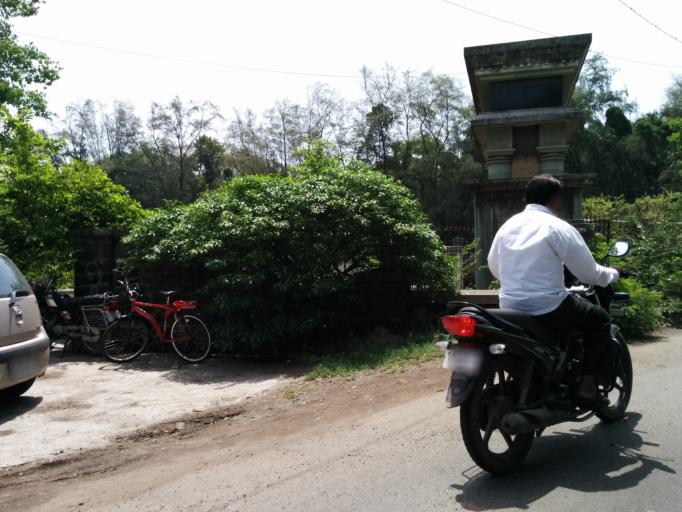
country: IN
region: Maharashtra
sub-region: Pune Division
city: Pune
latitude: 18.5330
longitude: 73.9162
